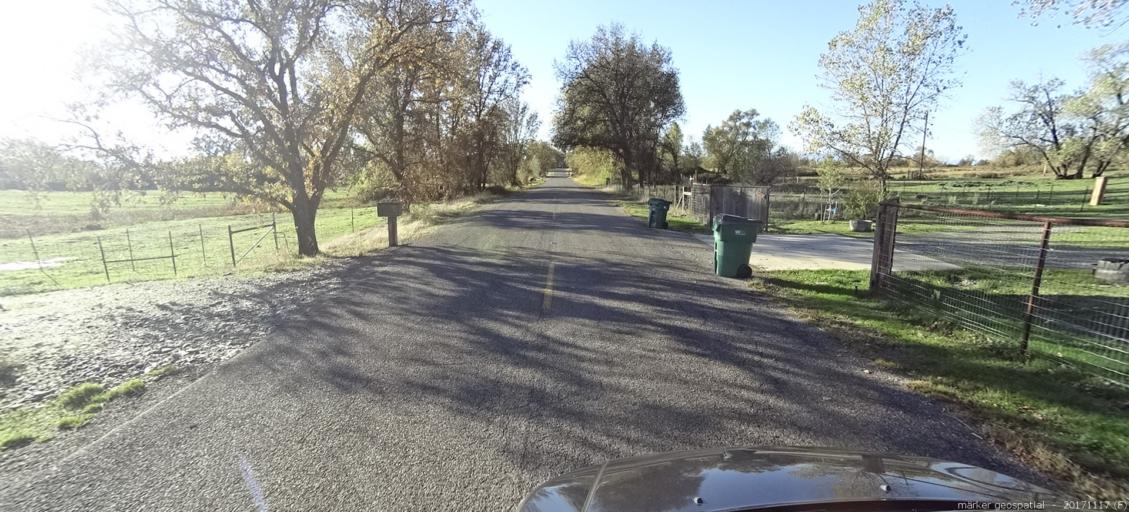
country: US
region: California
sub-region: Shasta County
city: Cottonwood
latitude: 40.3918
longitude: -122.2077
